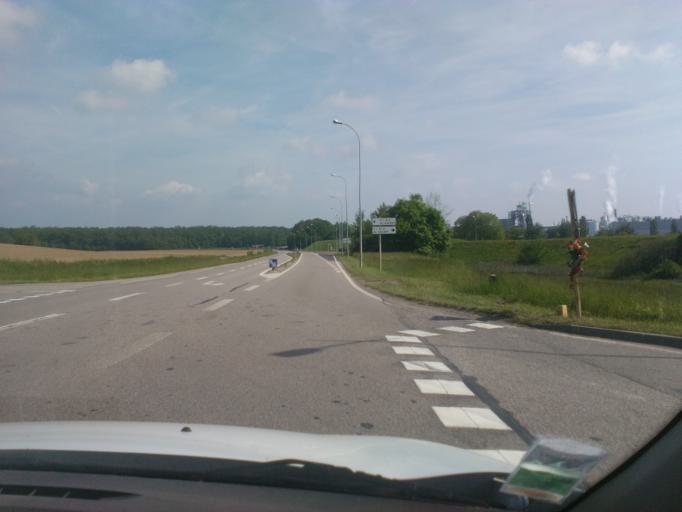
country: FR
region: Lorraine
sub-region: Departement des Vosges
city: Golbey
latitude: 48.2057
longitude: 6.4186
